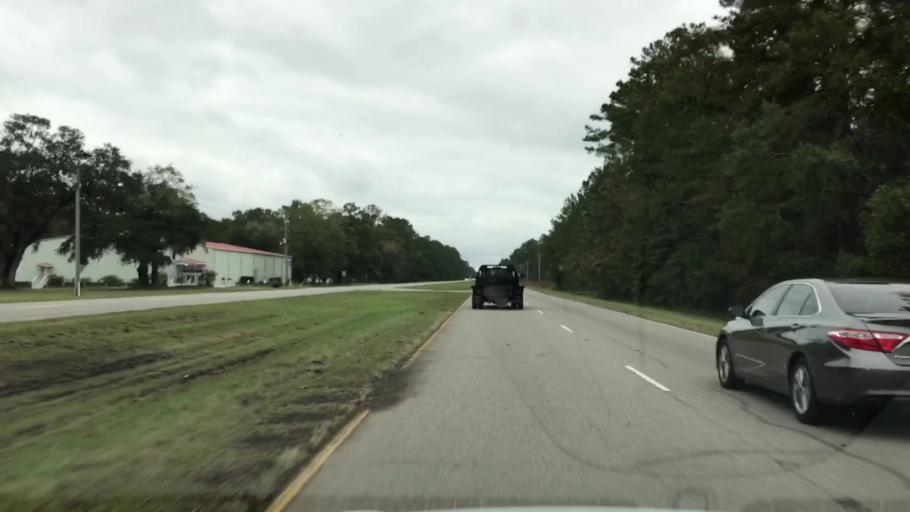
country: US
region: South Carolina
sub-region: Georgetown County
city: Georgetown
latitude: 33.3033
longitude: -79.3384
